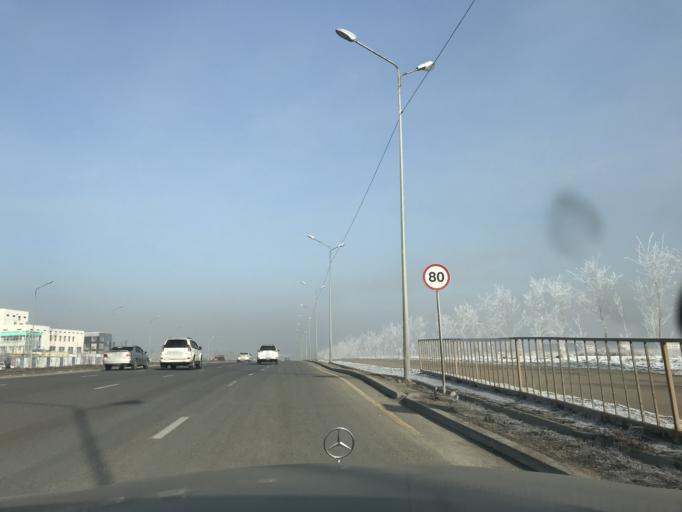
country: KZ
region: Almaty Oblysy
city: Burunday
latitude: 43.3154
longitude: 76.8342
